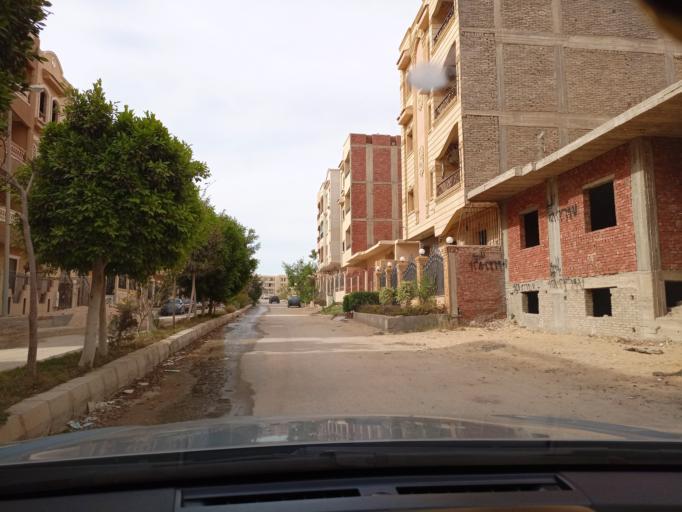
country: EG
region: Muhafazat al Qalyubiyah
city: Al Khankah
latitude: 30.2587
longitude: 31.4785
